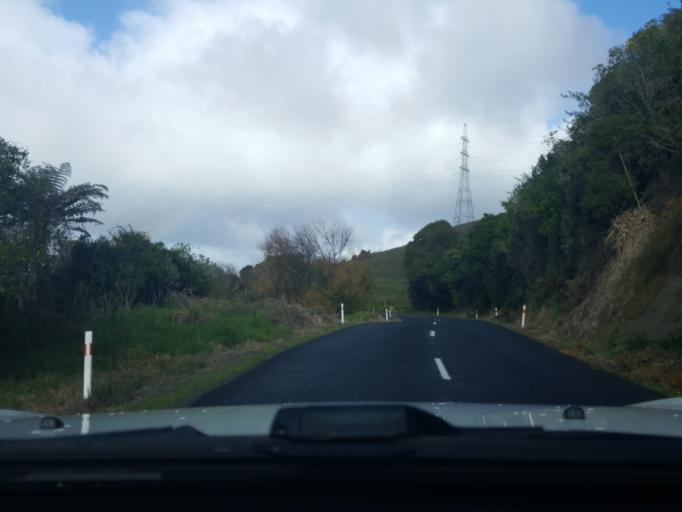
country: NZ
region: Waikato
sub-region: Waikato District
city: Te Kauwhata
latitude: -37.4065
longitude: 175.0597
